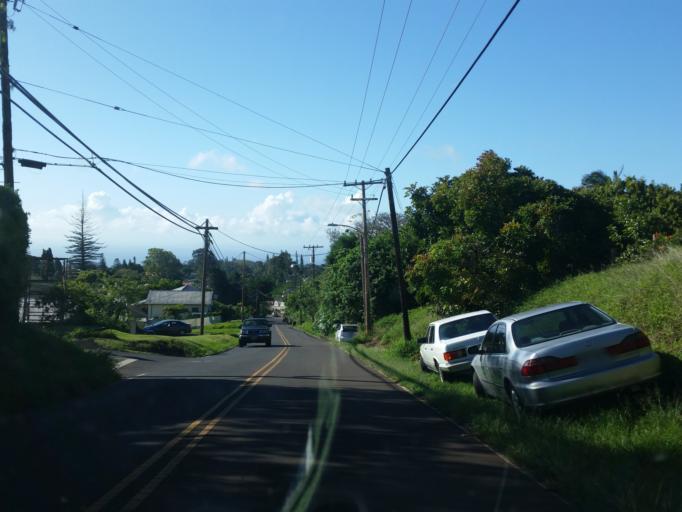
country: US
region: Hawaii
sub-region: Maui County
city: Makawao
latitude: 20.8516
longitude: -156.3092
